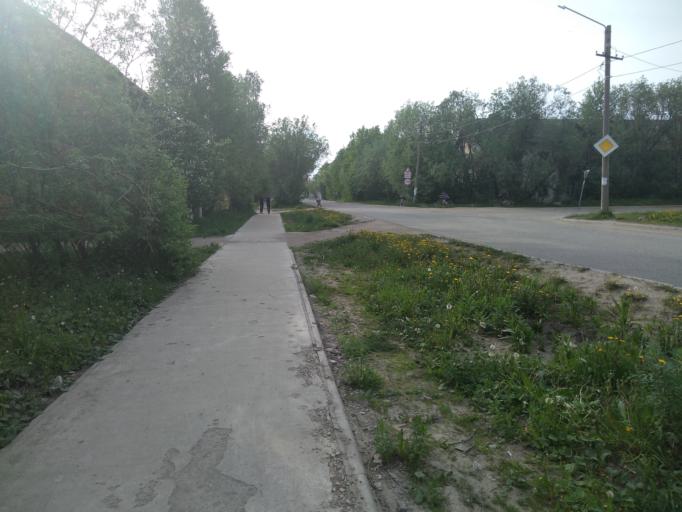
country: RU
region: Komi Republic
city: Pechora
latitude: 65.1453
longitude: 57.2258
